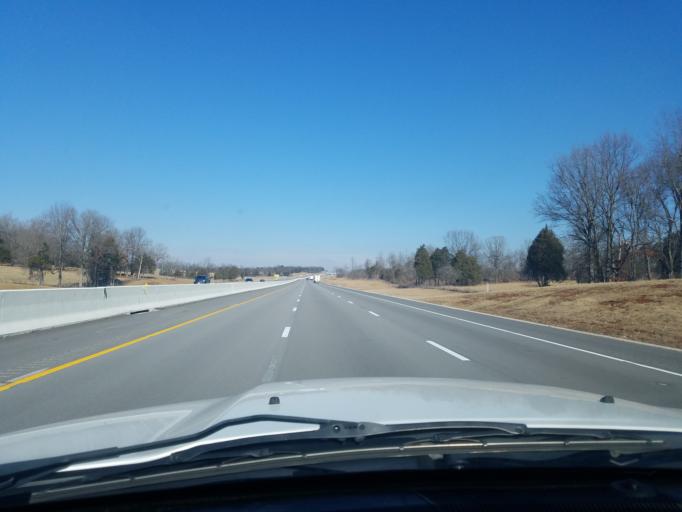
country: US
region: Kentucky
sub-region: Hart County
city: Munfordville
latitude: 37.4318
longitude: -85.8833
